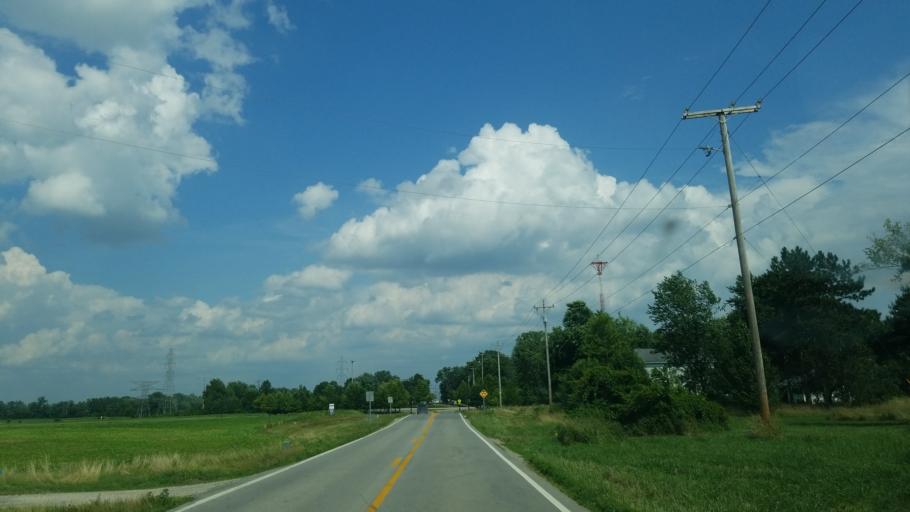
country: US
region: Ohio
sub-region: Delaware County
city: Powell
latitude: 40.2165
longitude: -83.0997
